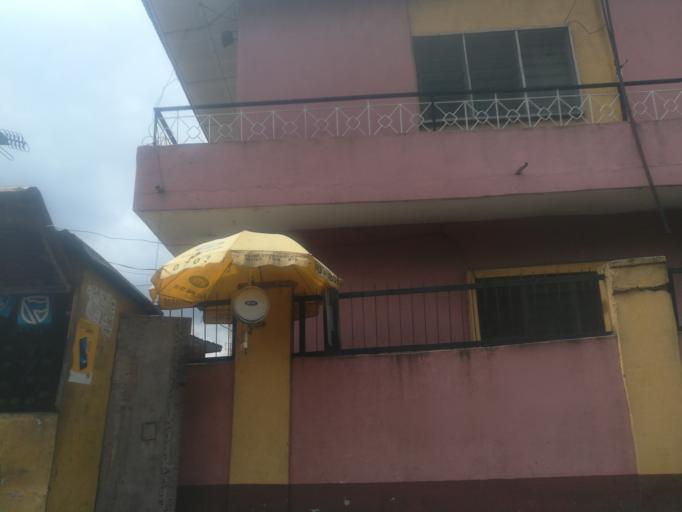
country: NG
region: Lagos
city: Ojota
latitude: 6.5951
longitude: 3.3894
